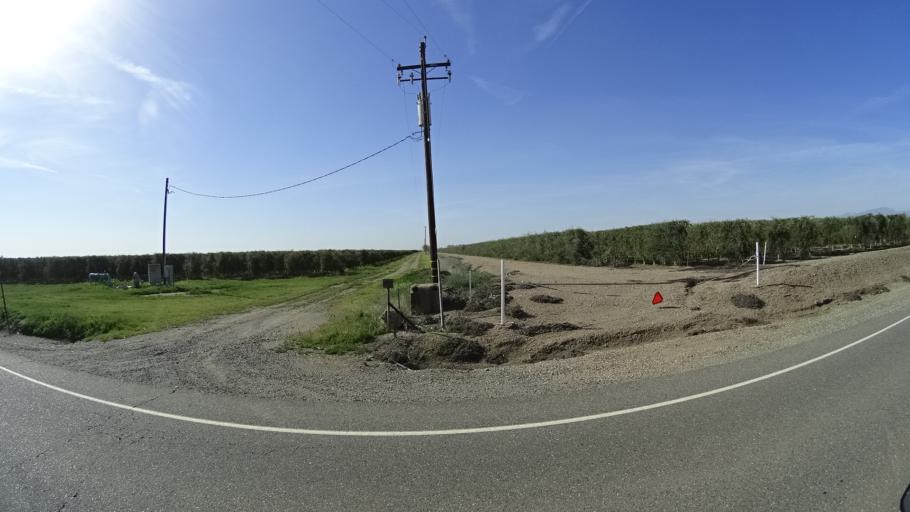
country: US
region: California
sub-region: Glenn County
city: Willows
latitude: 39.6246
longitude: -122.2318
